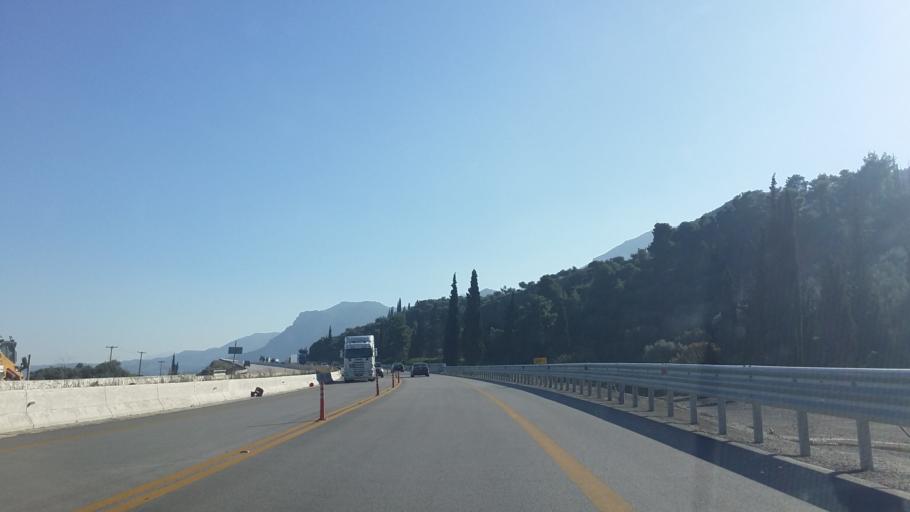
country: GR
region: West Greece
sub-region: Nomos Achaias
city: Temeni
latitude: 38.2064
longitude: 22.1380
